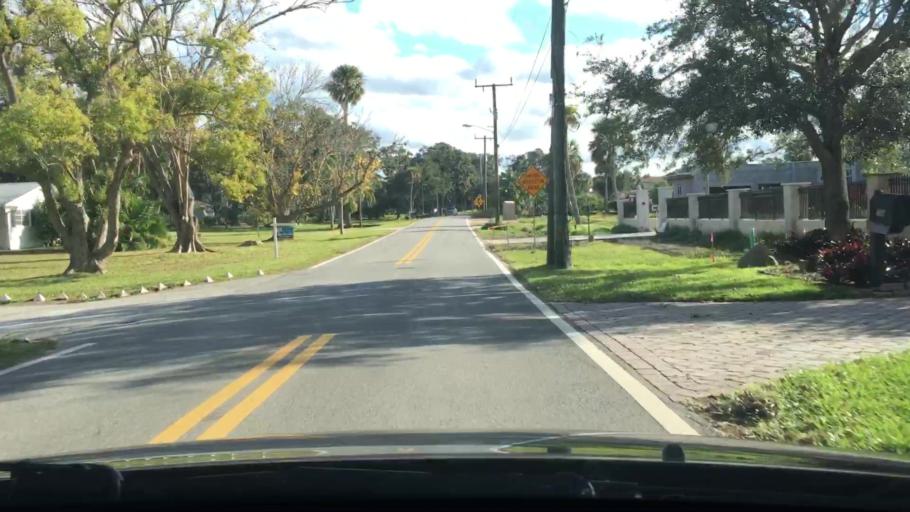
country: US
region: Florida
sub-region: Volusia County
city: Ormond Beach
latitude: 29.3067
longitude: -81.0558
